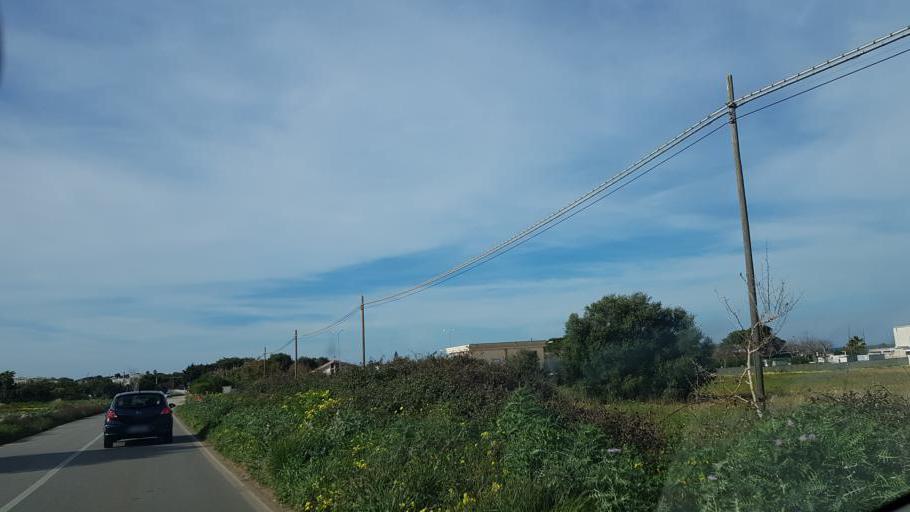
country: IT
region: Apulia
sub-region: Provincia di Brindisi
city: Fasano
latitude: 40.9016
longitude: 17.3525
